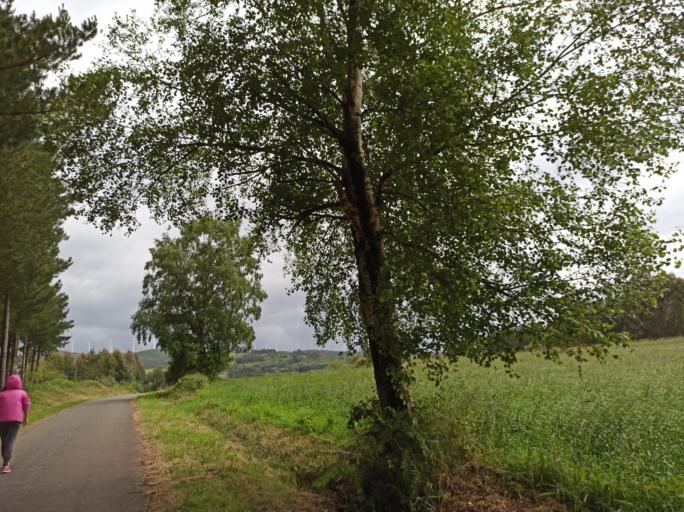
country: ES
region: Galicia
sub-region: Provincia de Pontevedra
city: Silleda
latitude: 42.7630
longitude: -8.1602
